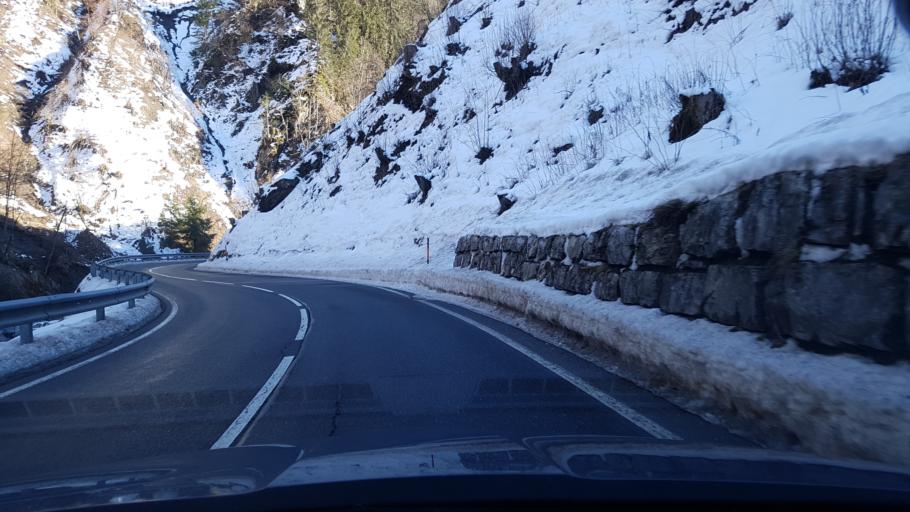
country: AT
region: Salzburg
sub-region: Politischer Bezirk Zell am See
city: Lend
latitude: 47.3103
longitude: 13.0324
